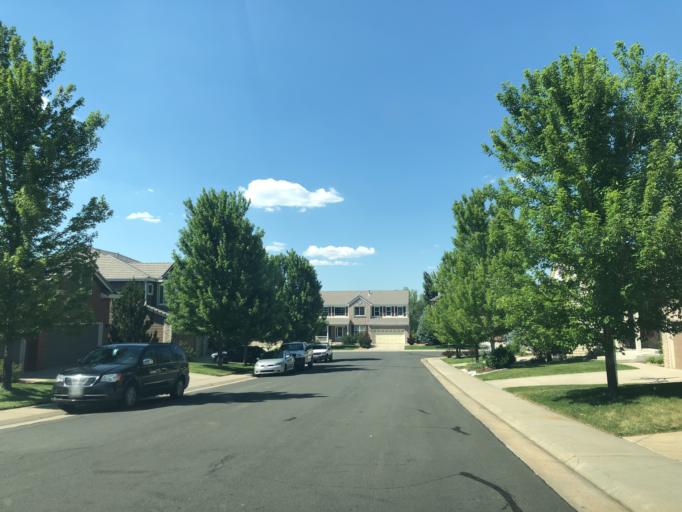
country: US
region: Colorado
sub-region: Arapahoe County
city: Dove Valley
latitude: 39.6084
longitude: -104.7877
